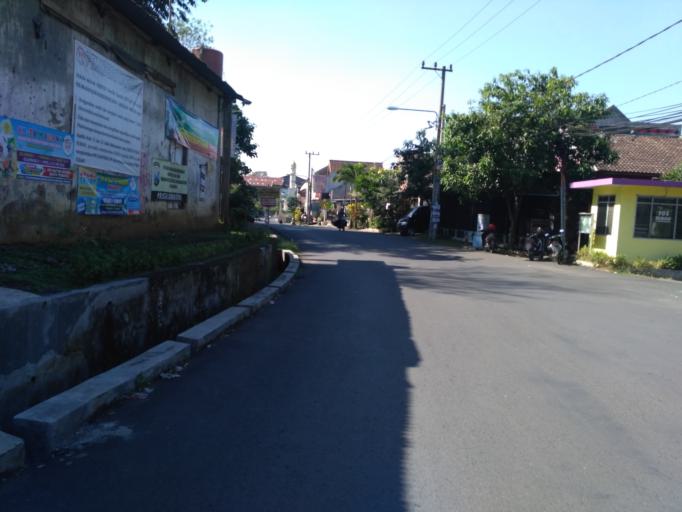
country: ID
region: East Java
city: Singosari
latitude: -7.9048
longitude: 112.6611
